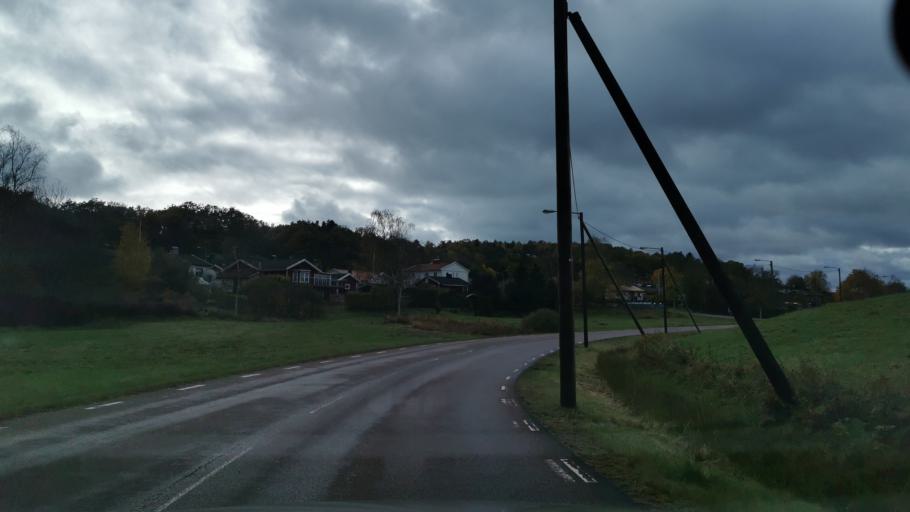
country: SE
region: Vaestra Goetaland
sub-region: Partille Kommun
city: Partille
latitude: 57.7242
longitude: 12.0912
